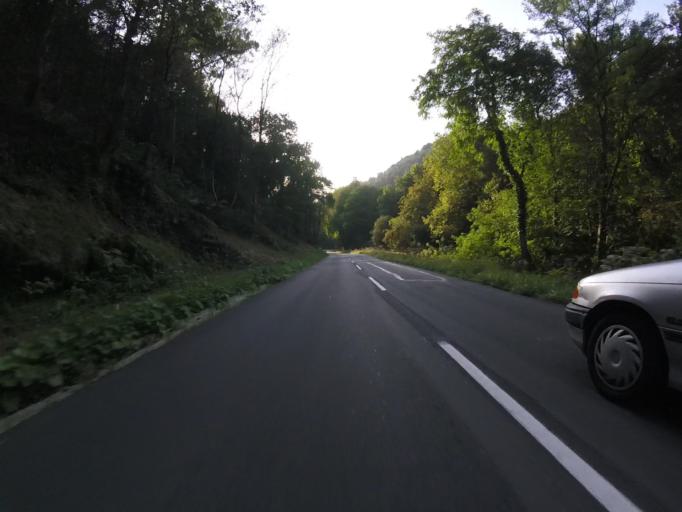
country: ES
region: Basque Country
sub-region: Provincia de Guipuzcoa
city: Lezo
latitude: 43.3278
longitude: -1.9042
